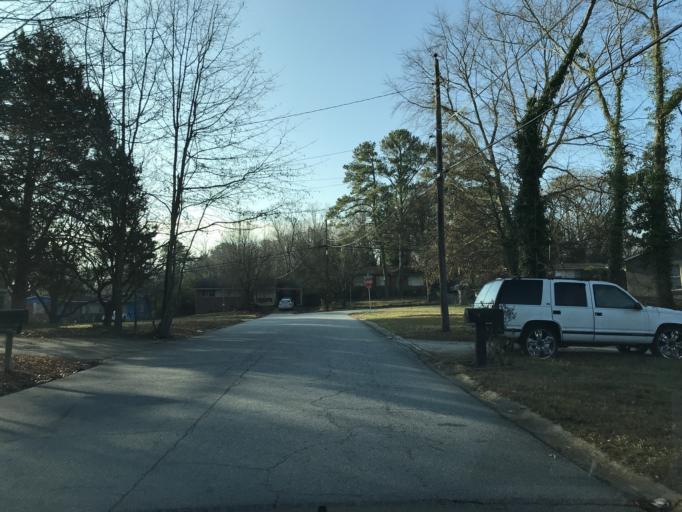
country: US
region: Georgia
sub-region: Fulton County
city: College Park
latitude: 33.6151
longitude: -84.4356
